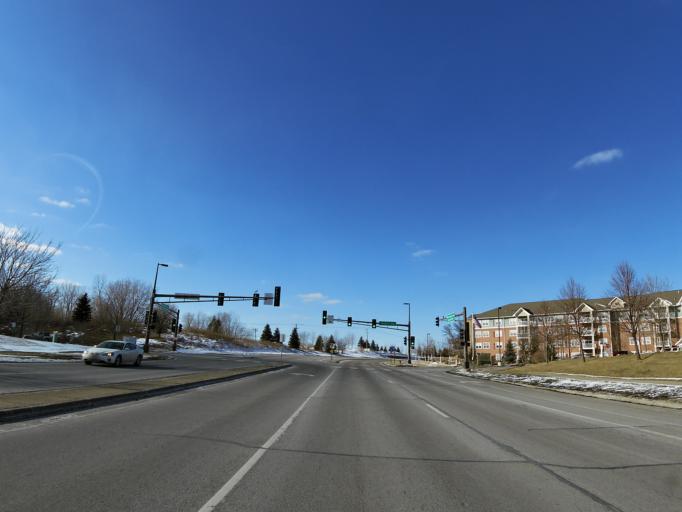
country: US
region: Minnesota
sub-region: Washington County
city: Woodbury
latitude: 44.9187
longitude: -92.9827
